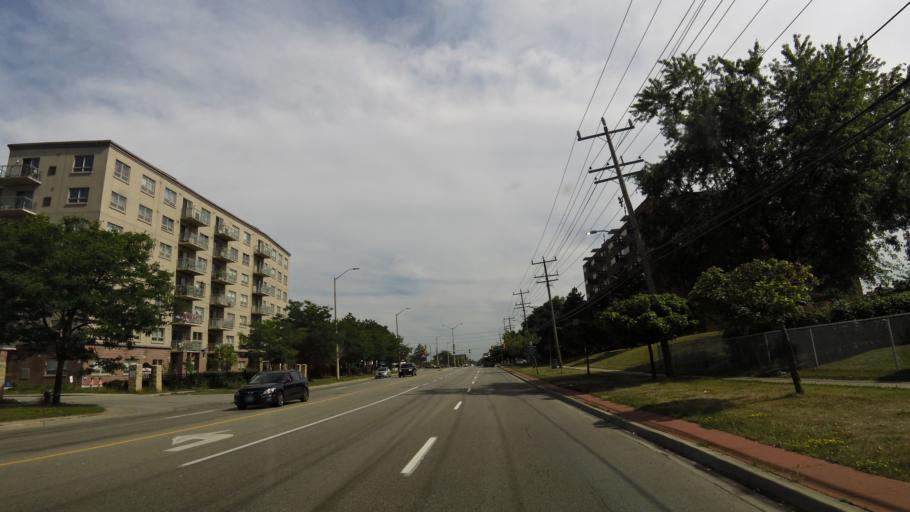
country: CA
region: Ontario
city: Etobicoke
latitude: 43.7220
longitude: -79.6433
